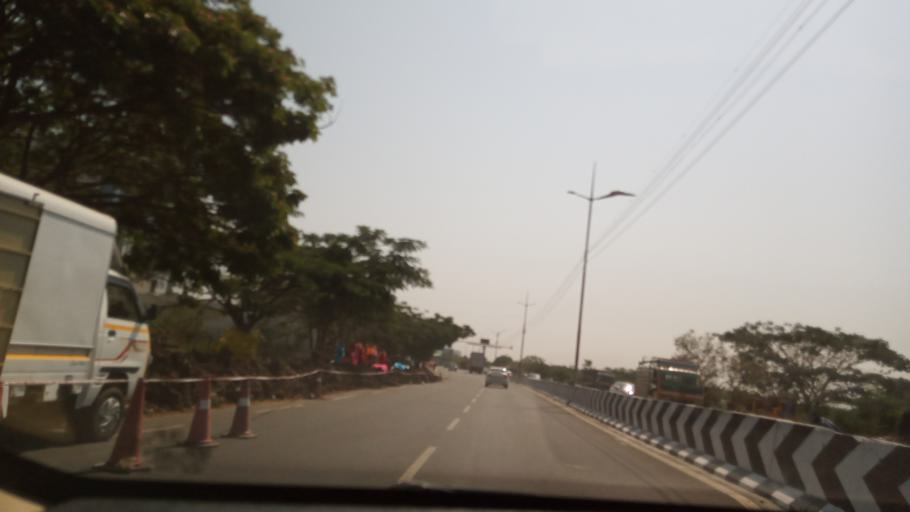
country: IN
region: Tamil Nadu
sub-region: Coimbatore
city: Irugur
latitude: 11.0577
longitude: 77.0732
